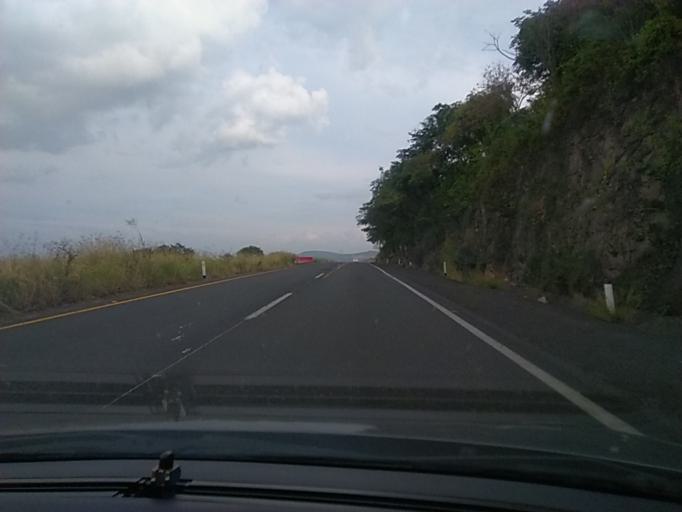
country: MX
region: Michoacan
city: Copandaro de Galeana
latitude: 19.8975
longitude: -101.2568
